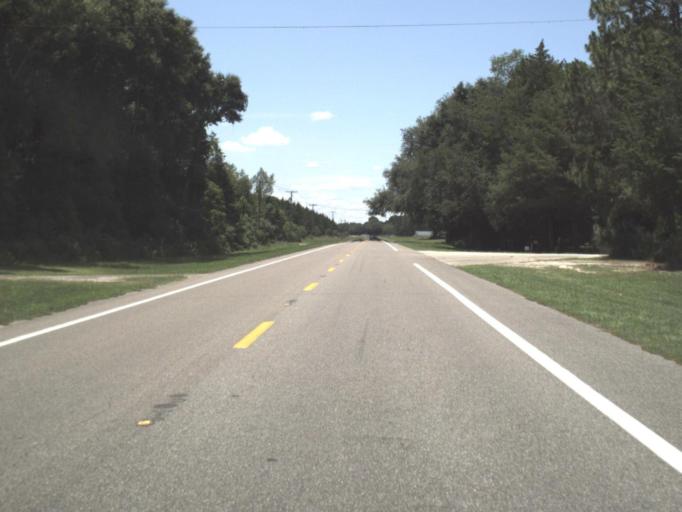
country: US
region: Florida
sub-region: Lafayette County
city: Mayo
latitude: 30.0451
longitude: -83.0788
